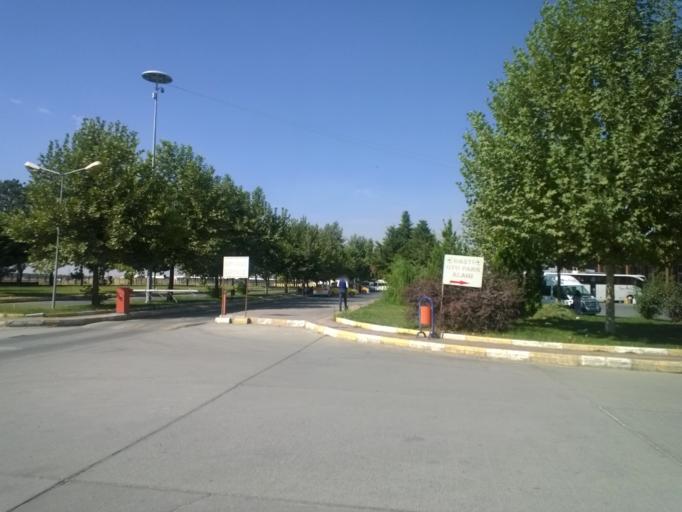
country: TR
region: Batman
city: Batman
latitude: 37.9062
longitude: 41.1121
